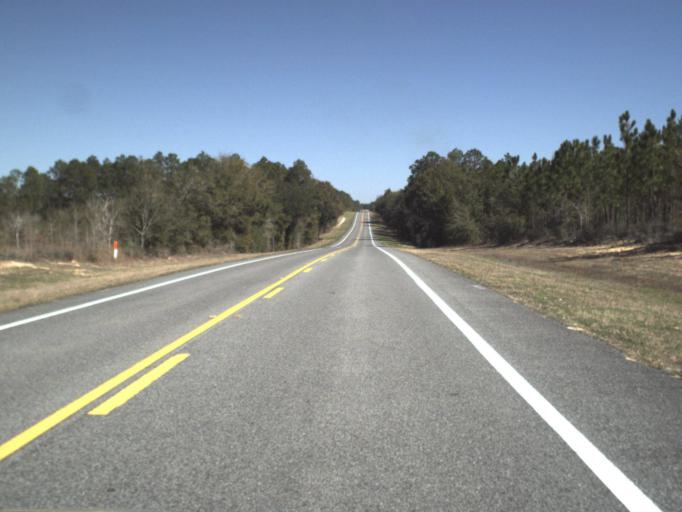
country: US
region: Florida
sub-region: Bay County
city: Youngstown
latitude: 30.4279
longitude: -85.5907
